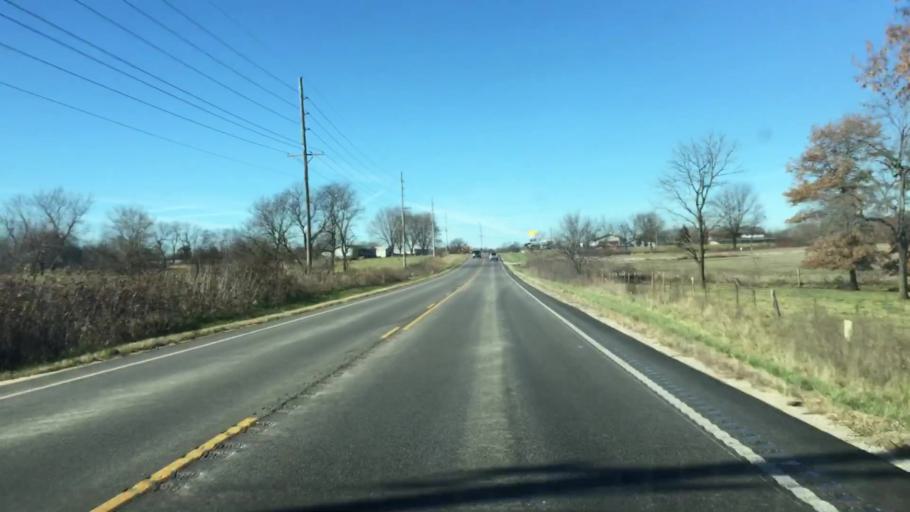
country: US
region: Missouri
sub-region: Miller County
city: Eldon
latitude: 38.3738
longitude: -92.6514
